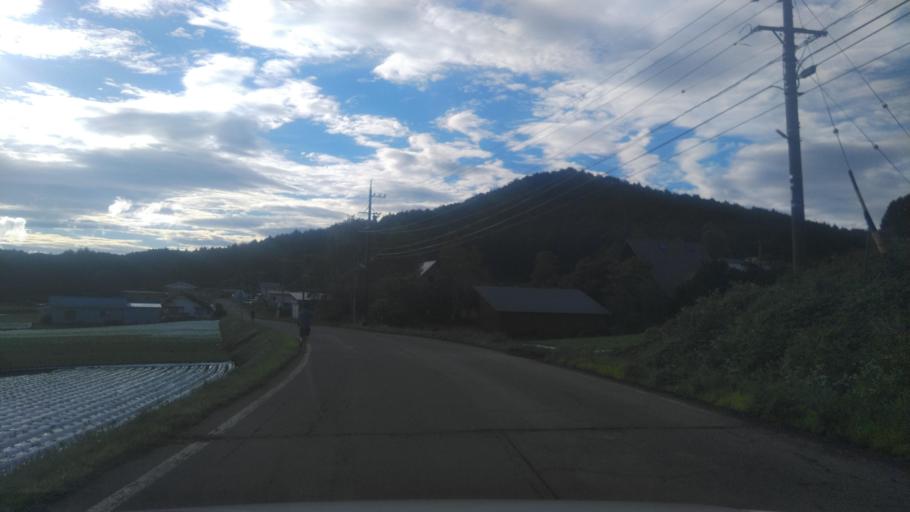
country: JP
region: Nagano
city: Suzaka
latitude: 36.5403
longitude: 138.3117
